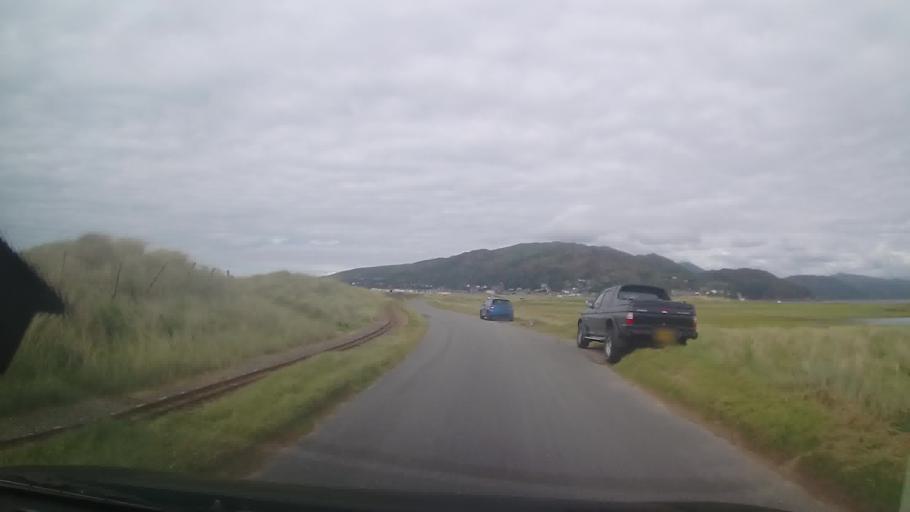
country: GB
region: Wales
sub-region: Gwynedd
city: Barmouth
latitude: 52.7061
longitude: -4.0584
